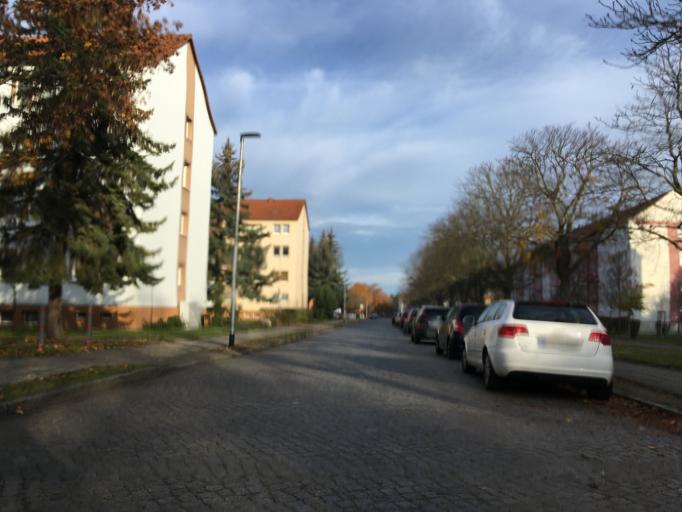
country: DE
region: Brandenburg
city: Luebben
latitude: 51.9465
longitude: 13.8851
